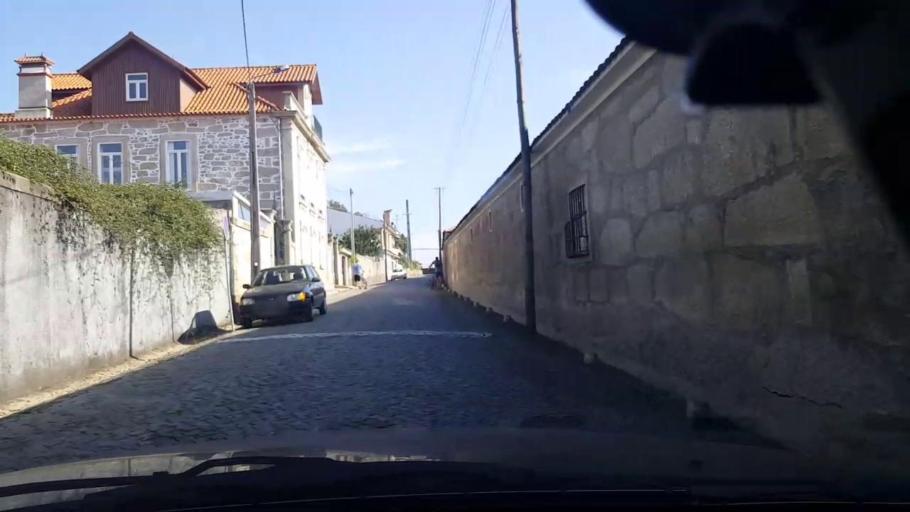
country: PT
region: Porto
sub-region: Maia
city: Gemunde
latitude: 41.2762
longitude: -8.6700
